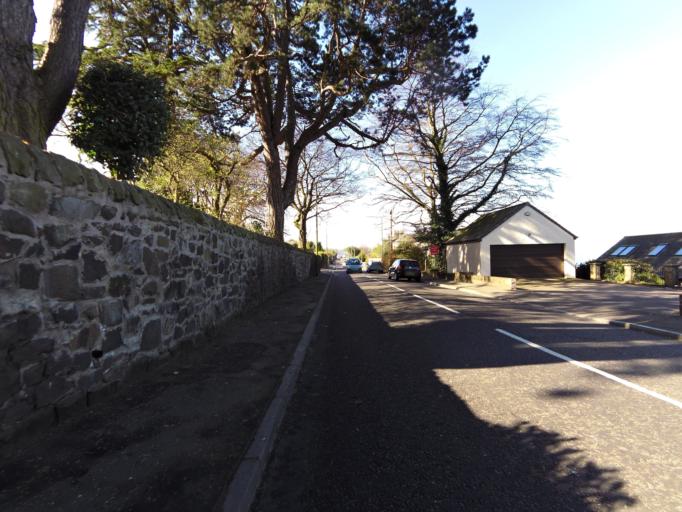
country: GB
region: Scotland
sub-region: Fife
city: Newport-On-Tay
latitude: 56.4460
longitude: -2.9355
